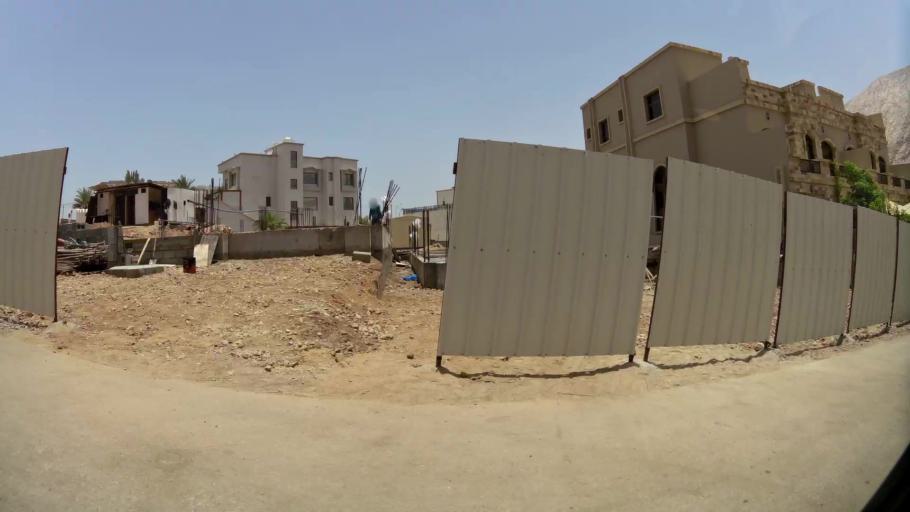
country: OM
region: Muhafazat Masqat
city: Bawshar
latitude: 23.5559
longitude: 58.4132
